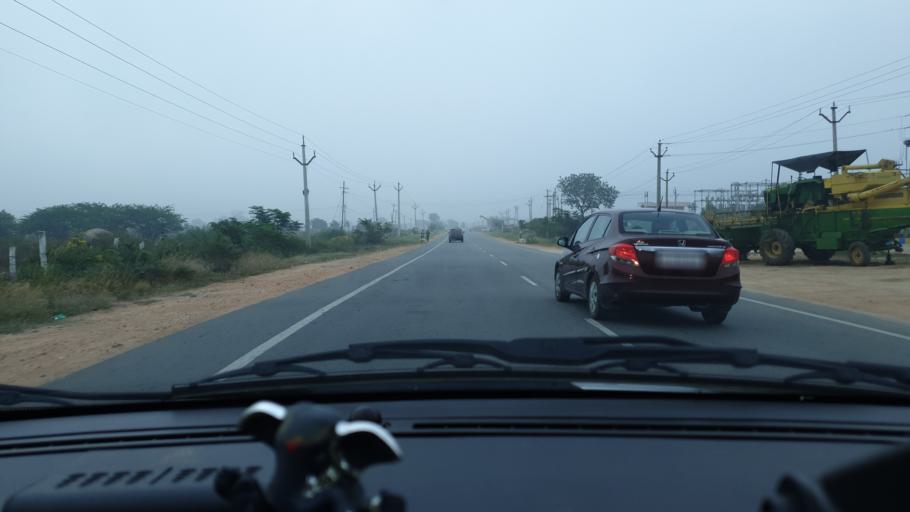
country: IN
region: Telangana
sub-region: Mahbubnagar
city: Farrukhnagar
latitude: 16.9305
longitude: 78.5280
